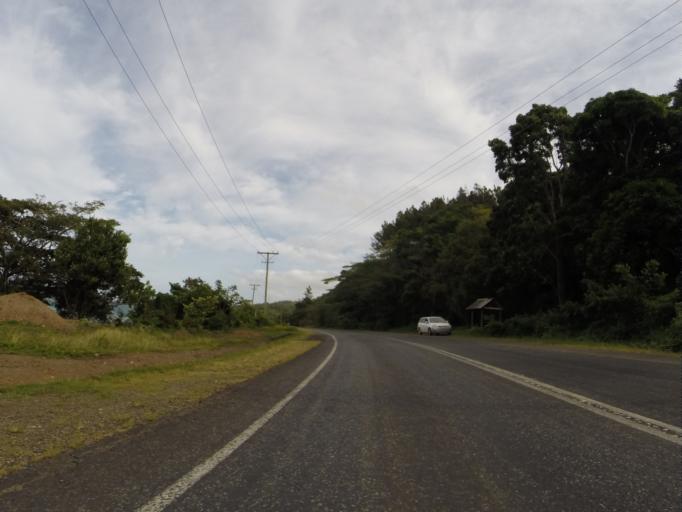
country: FJ
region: Western
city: Nadi
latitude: -18.1988
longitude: 177.6649
